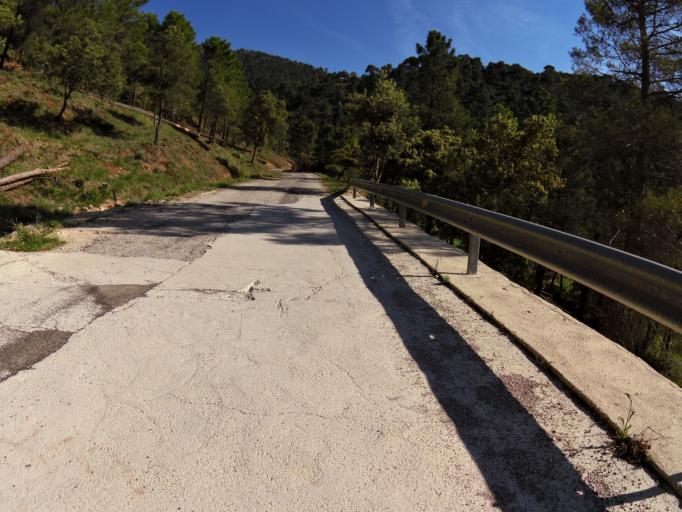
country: ES
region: Castille-La Mancha
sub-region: Provincia de Albacete
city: Riopar
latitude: 38.5216
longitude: -2.4557
